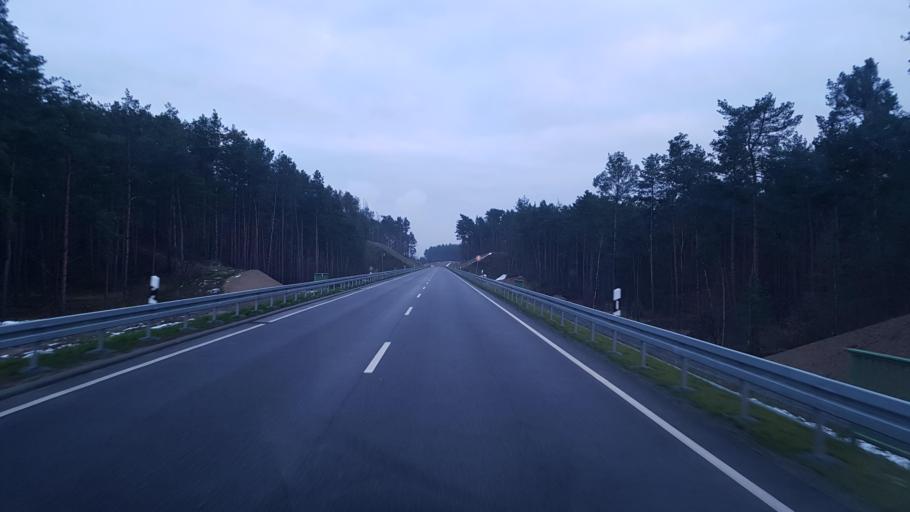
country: DE
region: Brandenburg
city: Wildau
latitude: 52.3206
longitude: 13.6580
